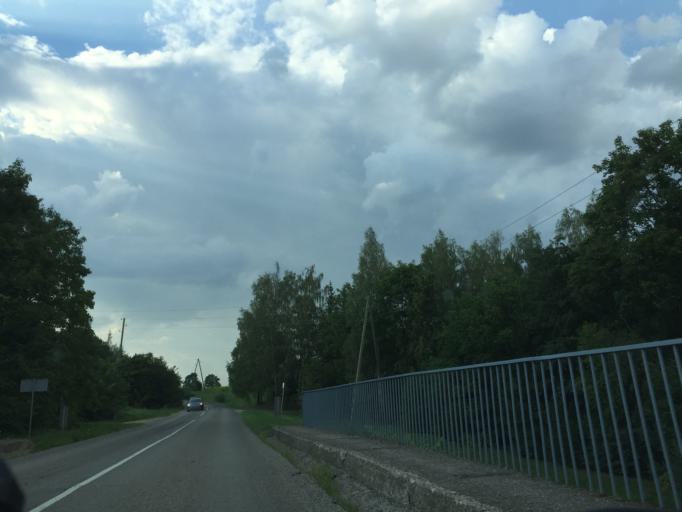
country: LV
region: Dobeles Rajons
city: Dobele
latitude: 56.6006
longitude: 23.3066
